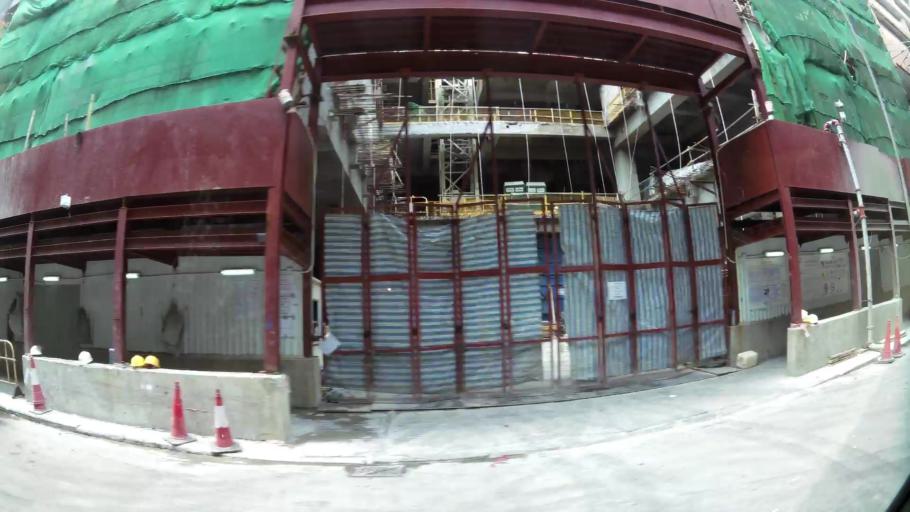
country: HK
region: Sham Shui Po
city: Sham Shui Po
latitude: 22.3390
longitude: 114.1525
